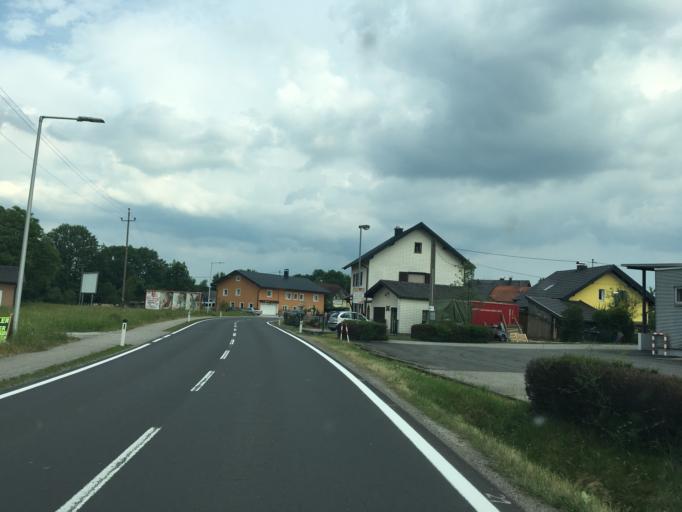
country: AT
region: Upper Austria
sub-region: Politischer Bezirk Braunau am Inn
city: Braunau am Inn
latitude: 48.1517
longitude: 13.1199
